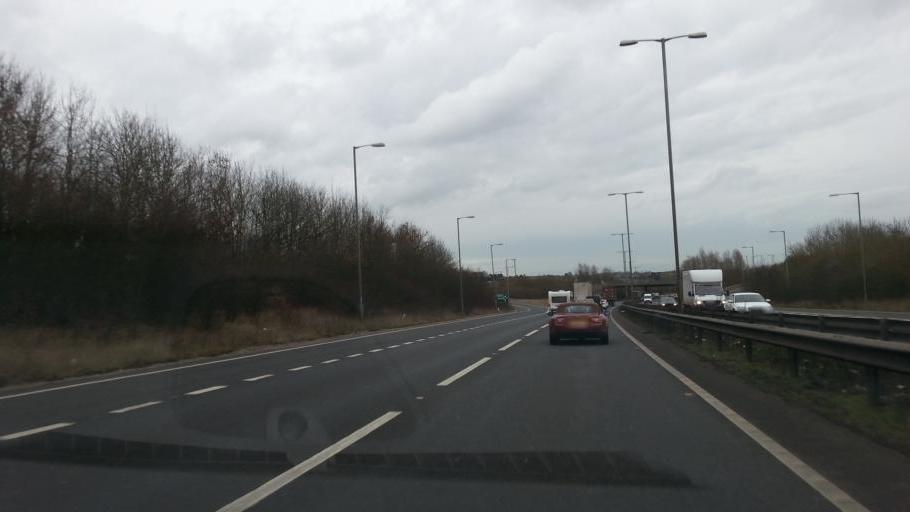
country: GB
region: England
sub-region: Northamptonshire
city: Rothwell
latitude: 52.4149
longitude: -0.8191
